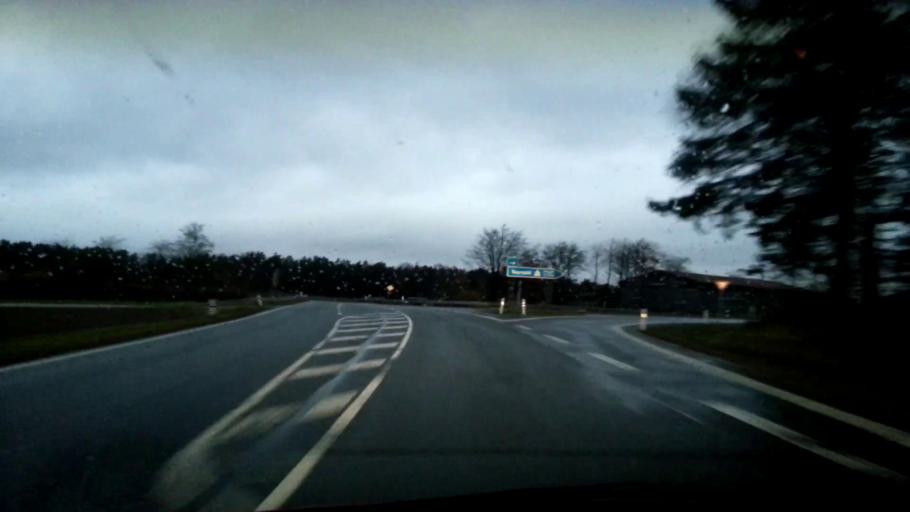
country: DE
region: Bavaria
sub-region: Upper Franconia
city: Wattendorf
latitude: 49.9877
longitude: 11.1193
